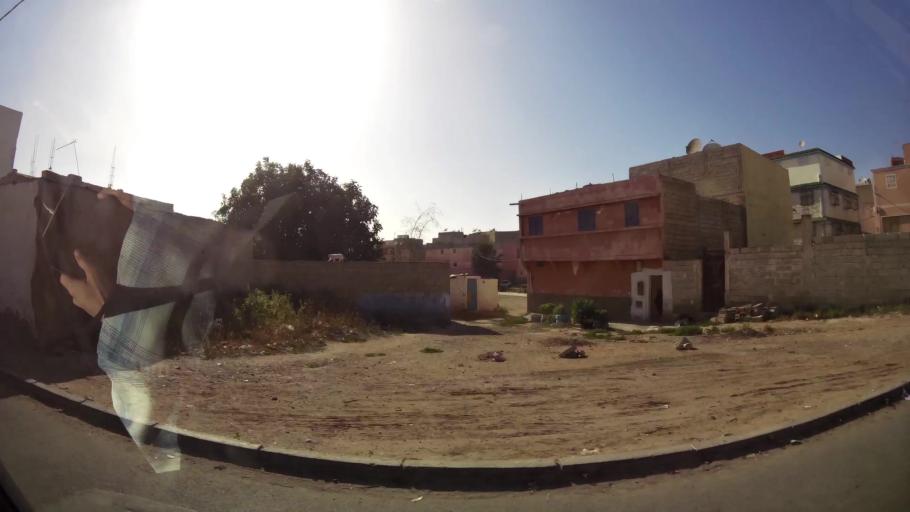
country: MA
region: Souss-Massa-Draa
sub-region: Inezgane-Ait Mellou
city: Inezgane
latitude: 30.3723
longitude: -9.5027
